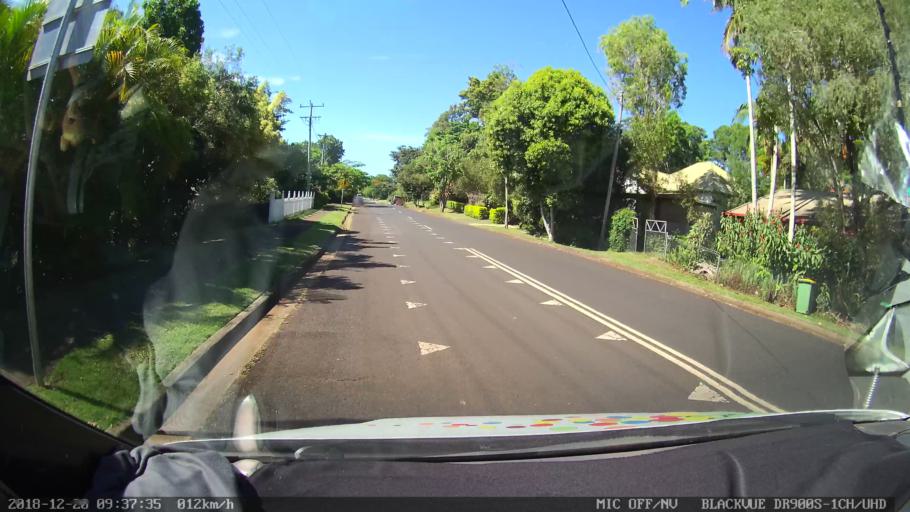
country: AU
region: New South Wales
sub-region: Lismore Municipality
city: Nimbin
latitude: -28.6850
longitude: 153.3152
